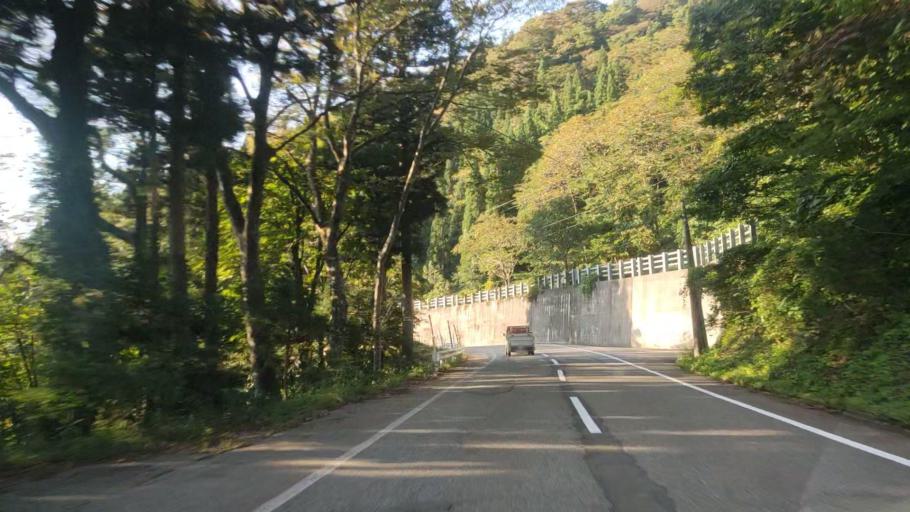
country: JP
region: Toyama
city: Yatsuomachi-higashikumisaka
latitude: 36.4982
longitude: 137.0257
